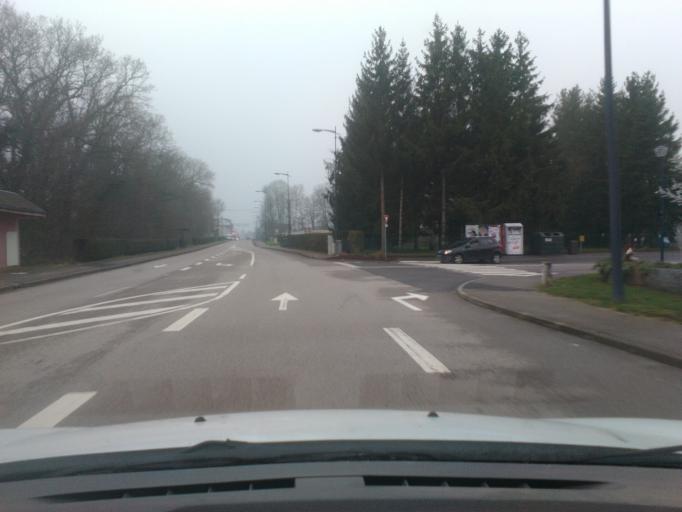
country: FR
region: Lorraine
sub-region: Departement des Vosges
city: Golbey
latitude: 48.2055
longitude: 6.4396
